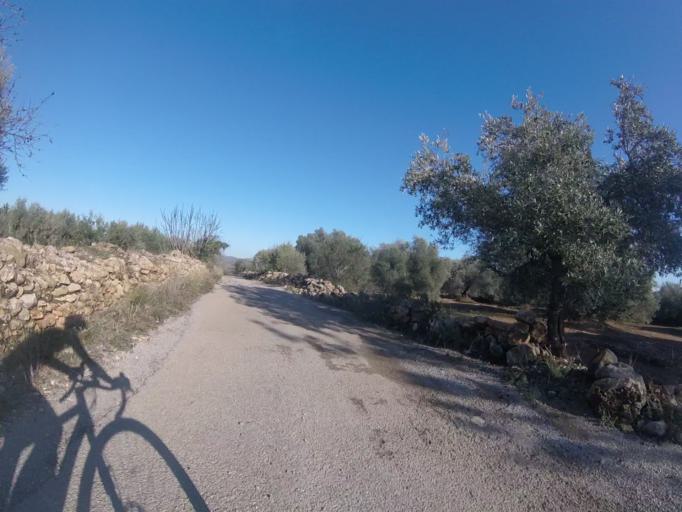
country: ES
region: Valencia
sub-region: Provincia de Castello
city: Sarratella
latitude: 40.2878
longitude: 0.0750
